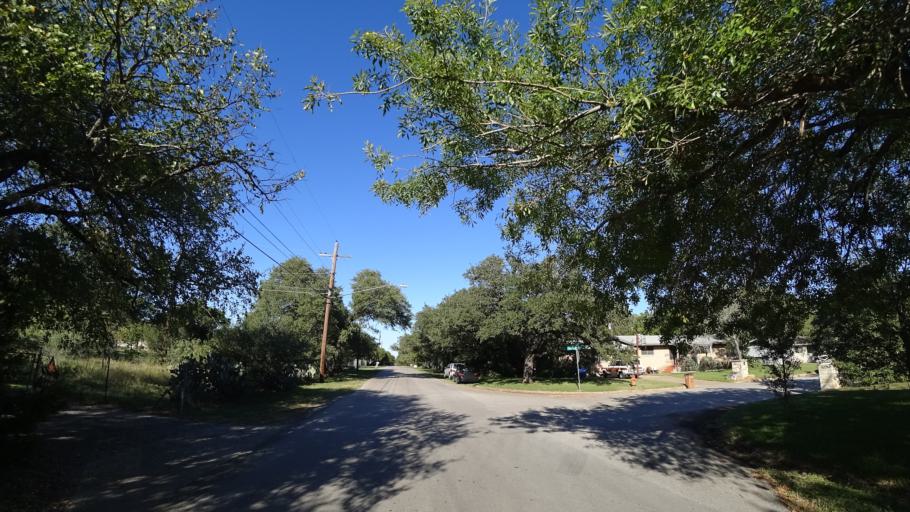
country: US
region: Texas
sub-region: Travis County
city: Rollingwood
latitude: 30.2357
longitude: -97.8100
